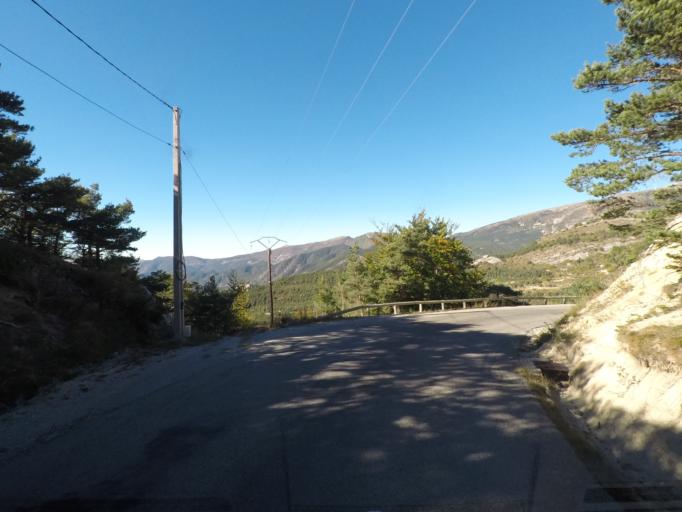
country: FR
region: Provence-Alpes-Cote d'Azur
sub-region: Departement des Hautes-Alpes
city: Serres
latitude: 44.4322
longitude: 5.5702
